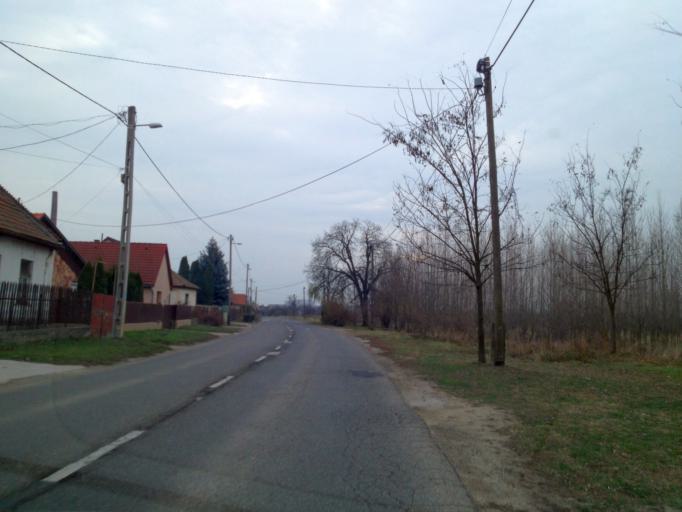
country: HU
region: Heves
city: Hatvan
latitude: 47.6851
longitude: 19.6887
